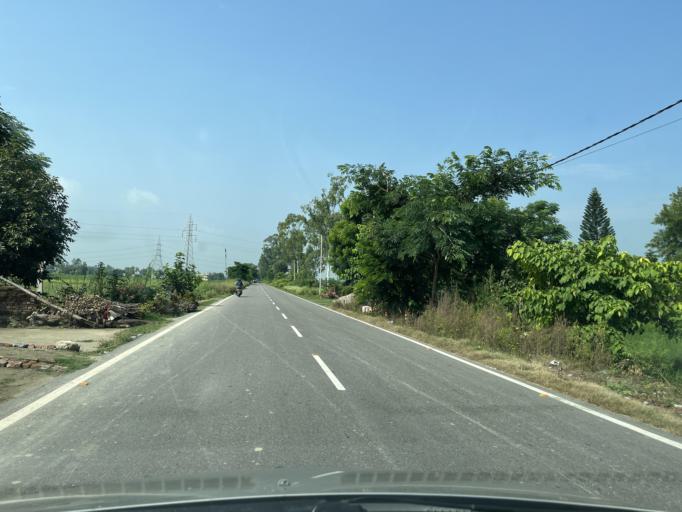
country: IN
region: Uttarakhand
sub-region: Udham Singh Nagar
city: Bazpur
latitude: 29.1971
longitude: 79.1991
